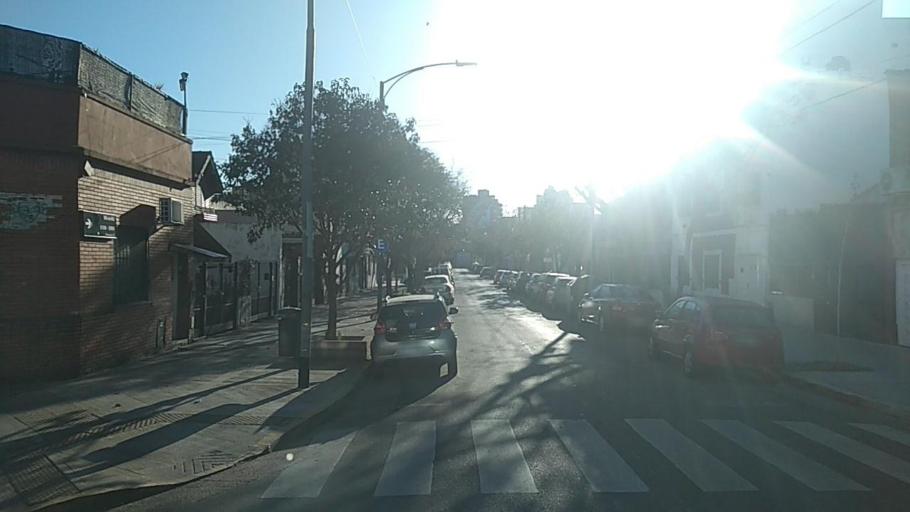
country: AR
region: Buenos Aires F.D.
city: Villa Santa Rita
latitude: -34.6236
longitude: -58.5068
